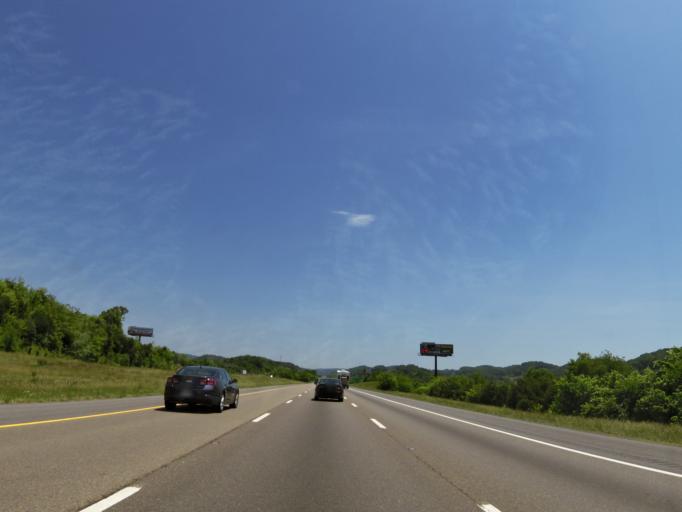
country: US
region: Tennessee
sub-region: Jefferson County
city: New Market
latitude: 35.9894
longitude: -83.5761
